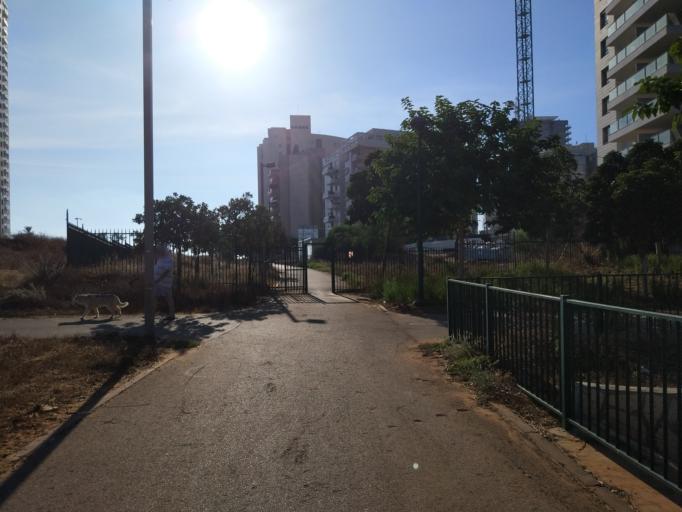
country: IL
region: Central District
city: Netanya
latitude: 32.2933
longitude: 34.8452
